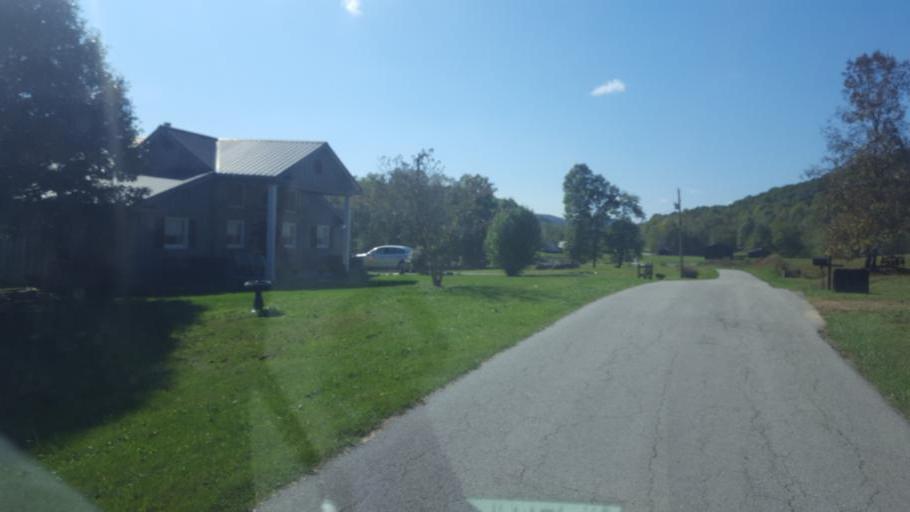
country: US
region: Kentucky
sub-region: Fleming County
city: Flemingsburg
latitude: 38.4446
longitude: -83.5548
